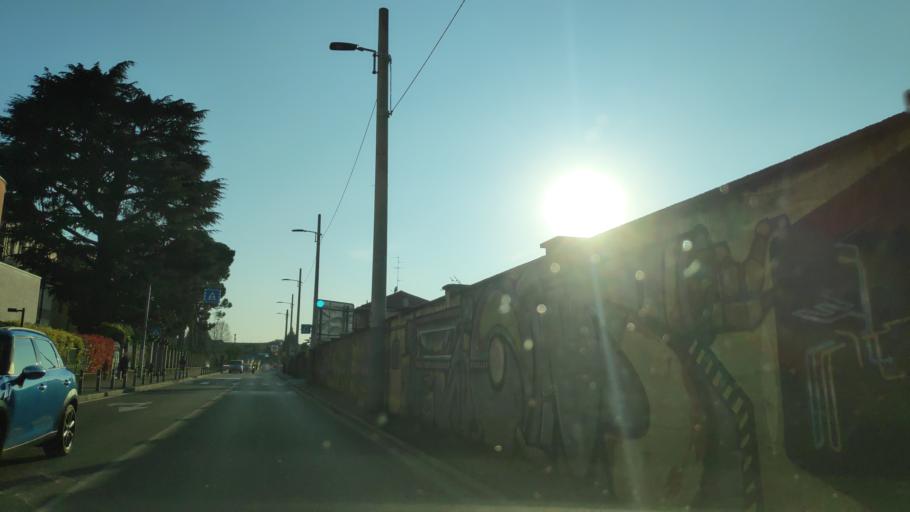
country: IT
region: Lombardy
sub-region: Provincia di Bergamo
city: Bergamo
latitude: 45.6897
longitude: 9.6798
